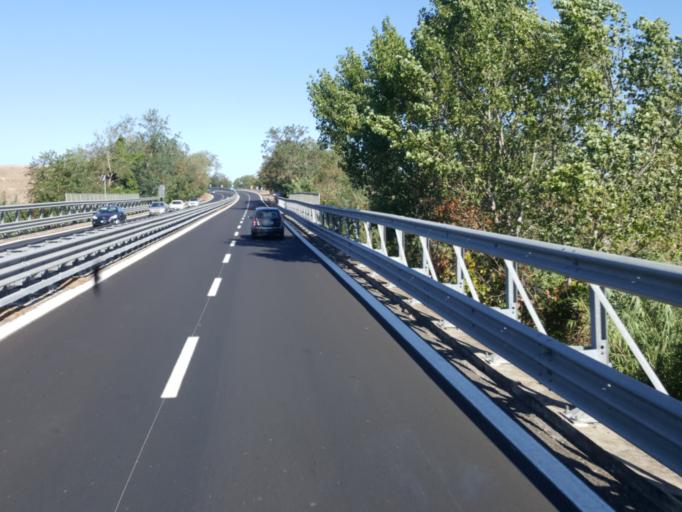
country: IT
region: Latium
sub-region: Provincia di Viterbo
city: Montalto di Castro
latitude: 42.3227
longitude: 11.6414
